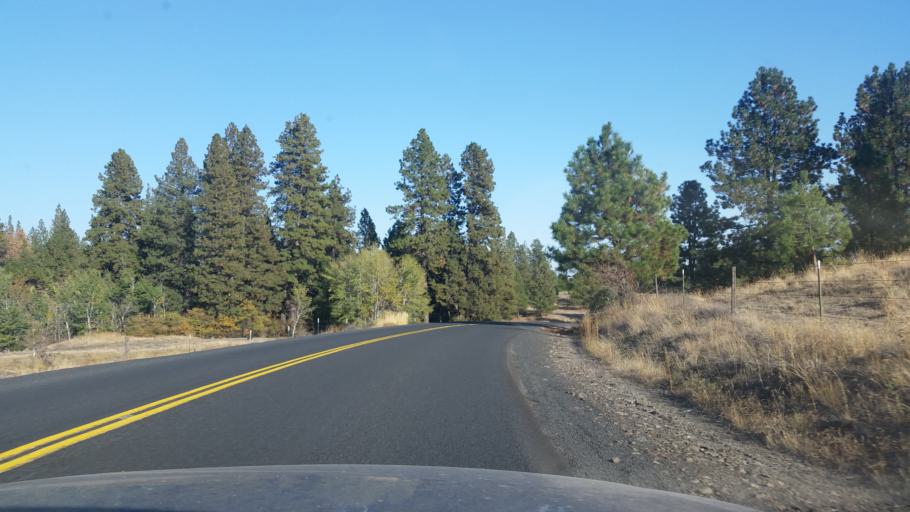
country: US
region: Washington
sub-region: Spokane County
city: Cheney
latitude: 47.3598
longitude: -117.6992
